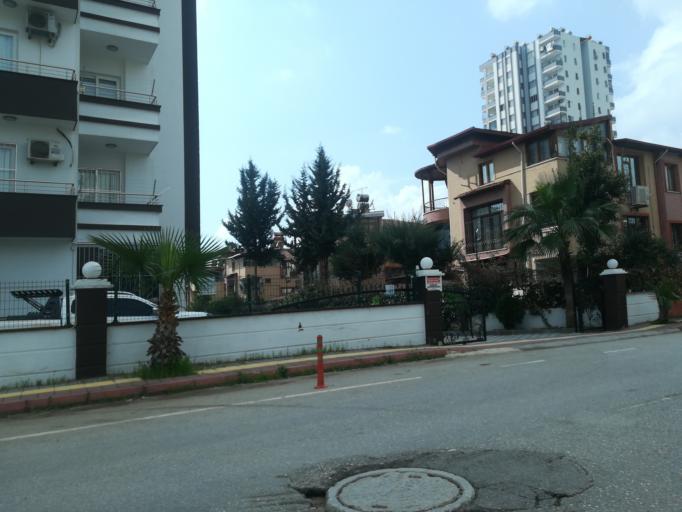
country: TR
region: Adana
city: Seyhan
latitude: 37.0249
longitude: 35.2735
